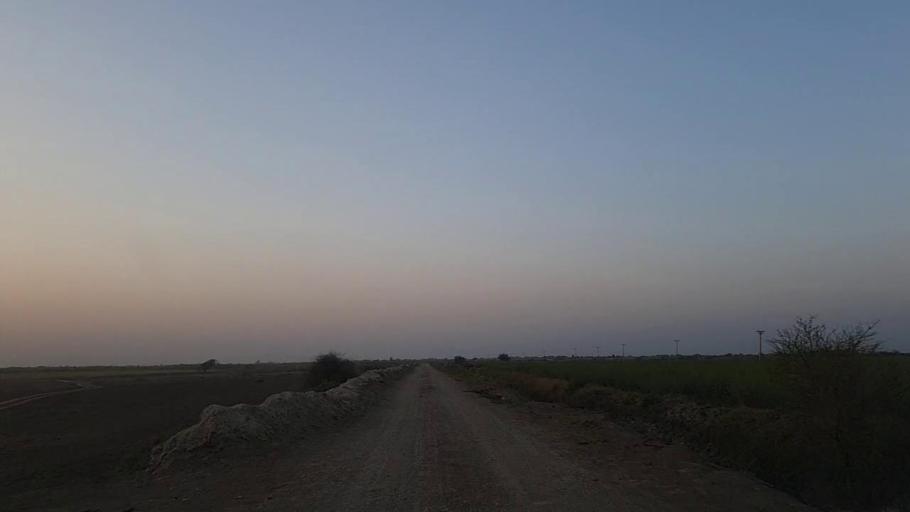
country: PK
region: Sindh
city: Naukot
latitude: 24.8946
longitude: 69.3599
